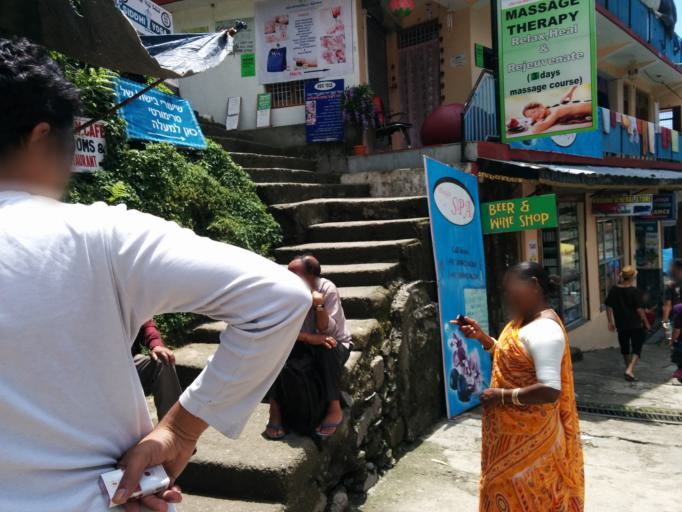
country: IN
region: Himachal Pradesh
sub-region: Kangra
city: Dharmsala
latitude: 32.2458
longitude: 76.3321
